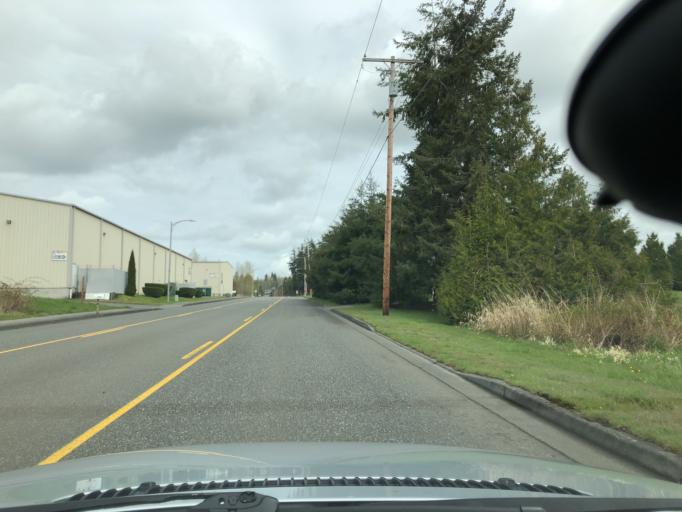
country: US
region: Washington
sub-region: Whatcom County
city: Blaine
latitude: 48.9846
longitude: -122.7254
